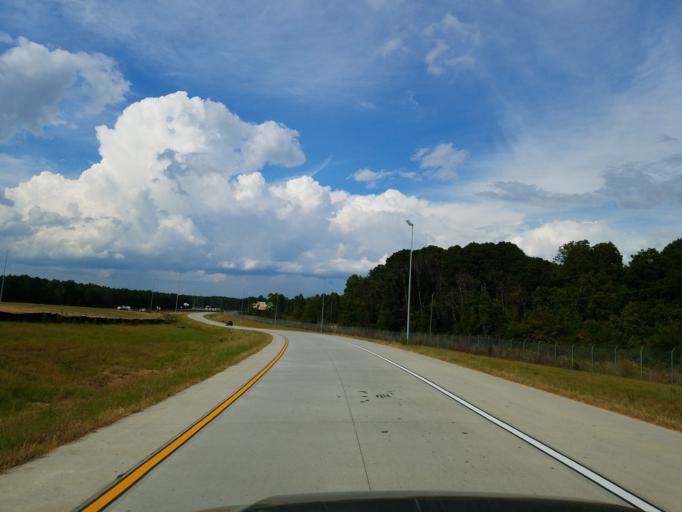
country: US
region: Georgia
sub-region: Tift County
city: Tifton
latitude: 31.5069
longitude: -83.5136
